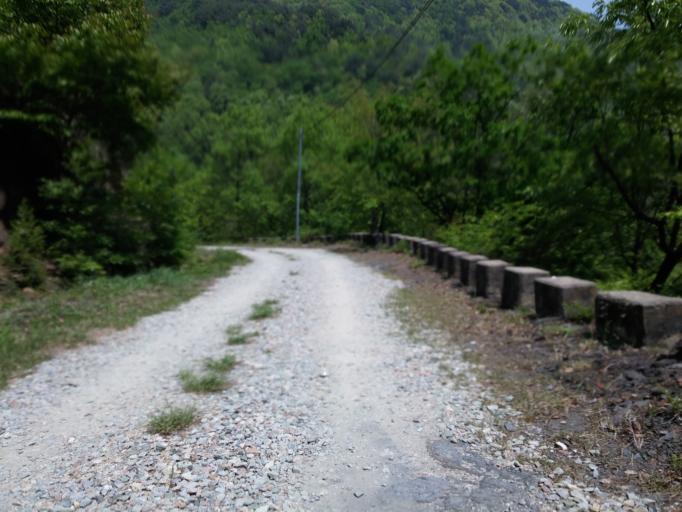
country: KR
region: Chungcheongbuk-do
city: Okcheon
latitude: 36.4160
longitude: 127.5949
